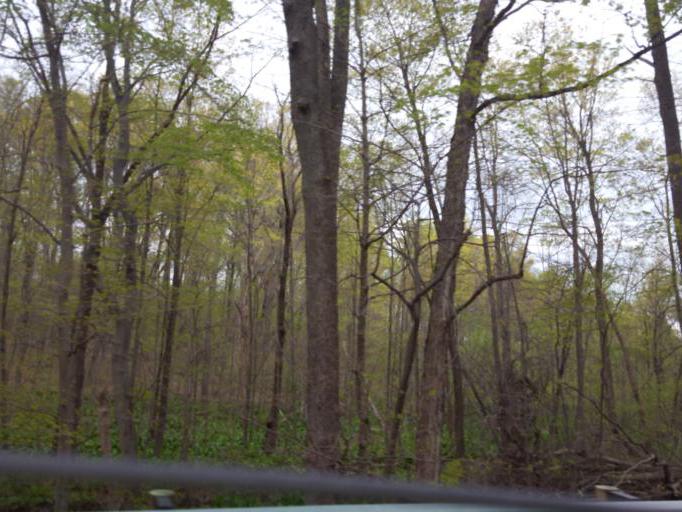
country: US
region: Ohio
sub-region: Richland County
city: Lexington
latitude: 40.7000
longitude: -82.6288
